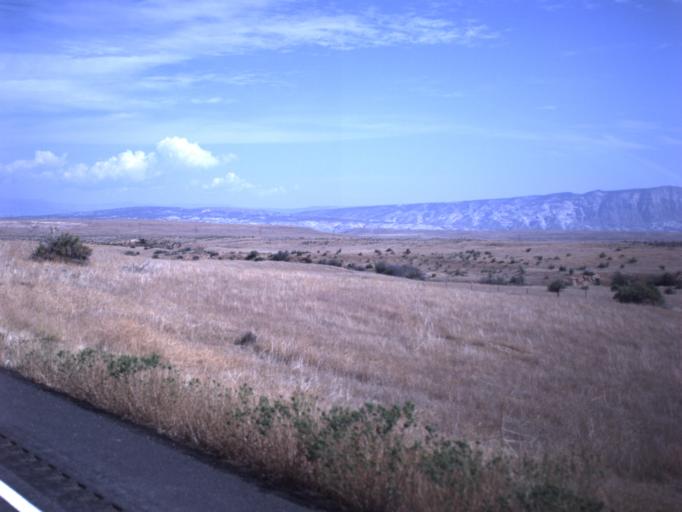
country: US
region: Utah
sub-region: Uintah County
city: Naples
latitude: 40.3480
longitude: -109.3045
